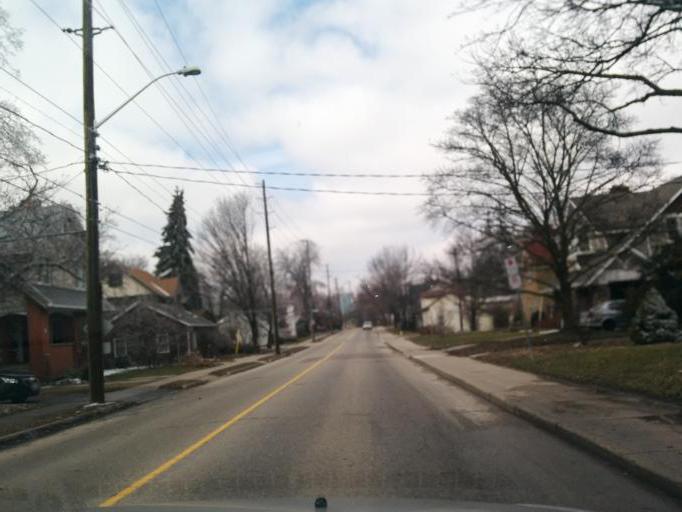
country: CA
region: Ontario
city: Waterloo
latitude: 43.4683
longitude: -80.5261
